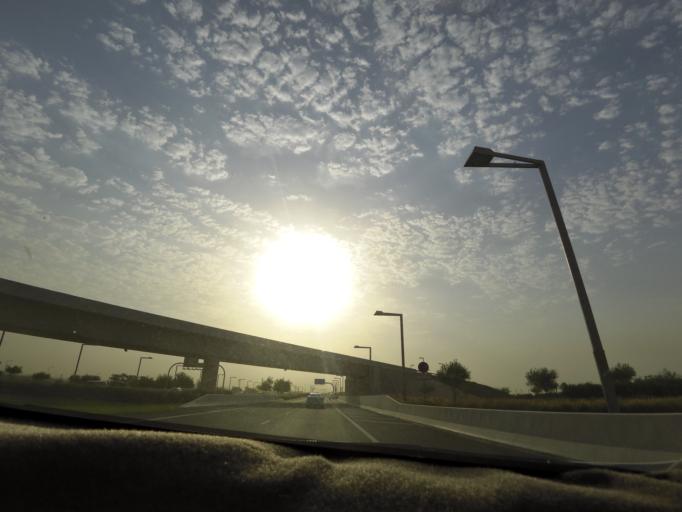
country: QA
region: Al Wakrah
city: Al Wakrah
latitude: 25.2469
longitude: 51.6062
